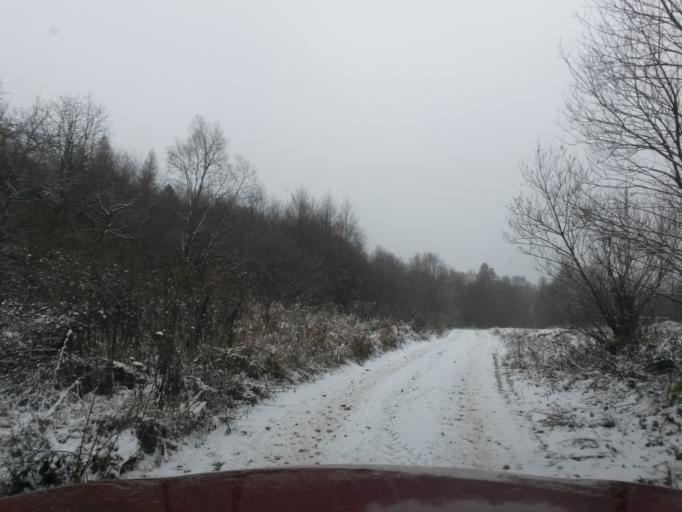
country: SK
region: Kosicky
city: Krompachy
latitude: 48.9882
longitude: 20.9958
